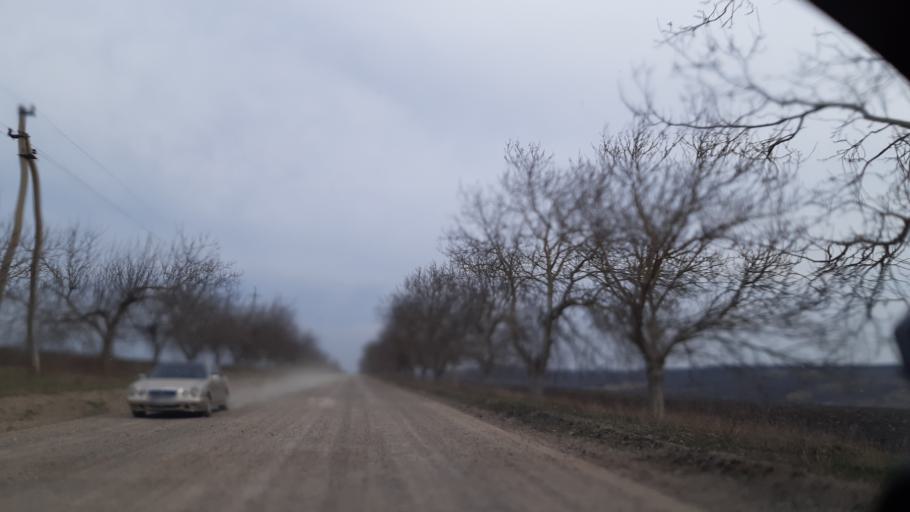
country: MD
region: Soldanesti
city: Soldanesti
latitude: 47.6953
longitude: 28.7323
